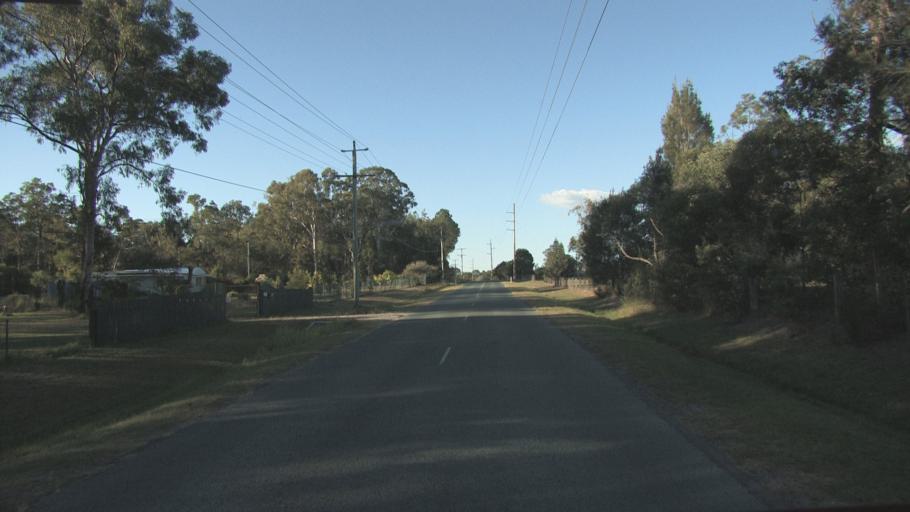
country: AU
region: Queensland
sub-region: Logan
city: Logan Reserve
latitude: -27.7312
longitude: 153.0932
